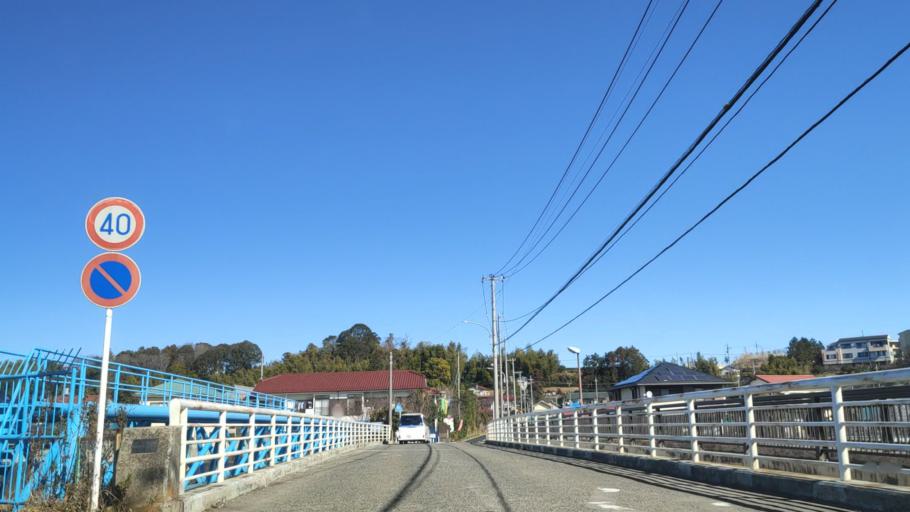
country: JP
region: Tokyo
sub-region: Machida-shi
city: Machida
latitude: 35.5187
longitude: 139.5359
